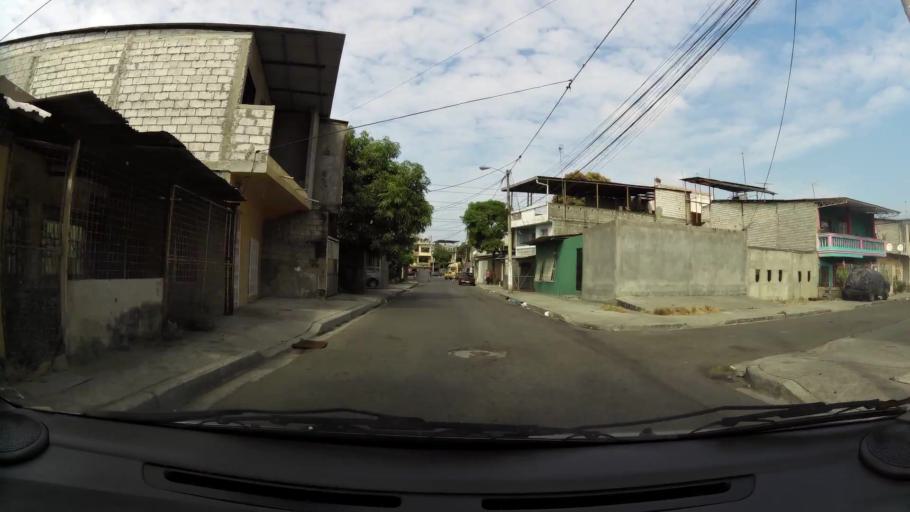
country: EC
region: Guayas
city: Guayaquil
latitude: -2.2594
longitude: -79.8817
